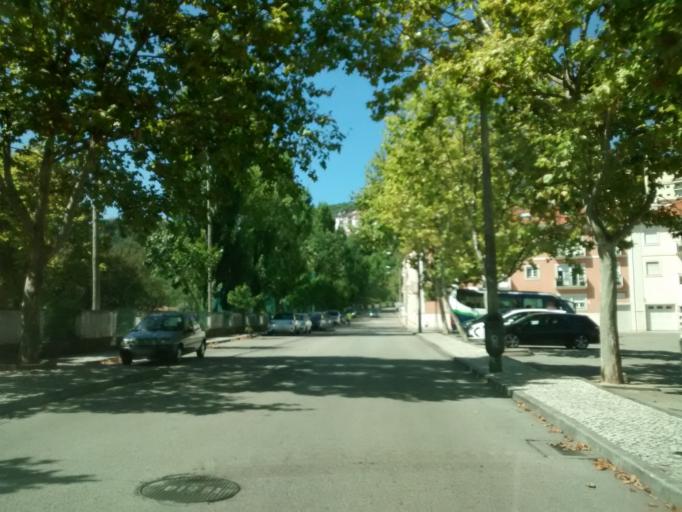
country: PT
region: Coimbra
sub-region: Coimbra
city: Coimbra
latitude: 40.2001
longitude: -8.4333
